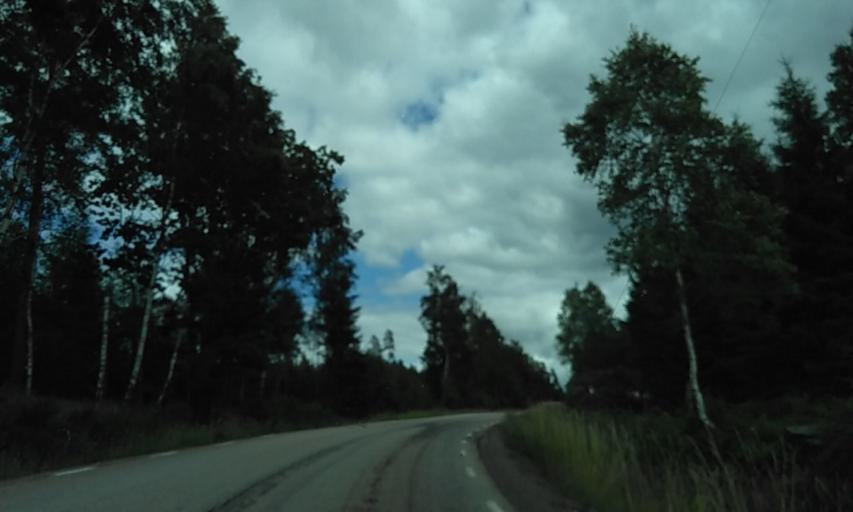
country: SE
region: Vaestra Goetaland
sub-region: Boras Kommun
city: Boras
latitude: 57.8145
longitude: 12.9238
